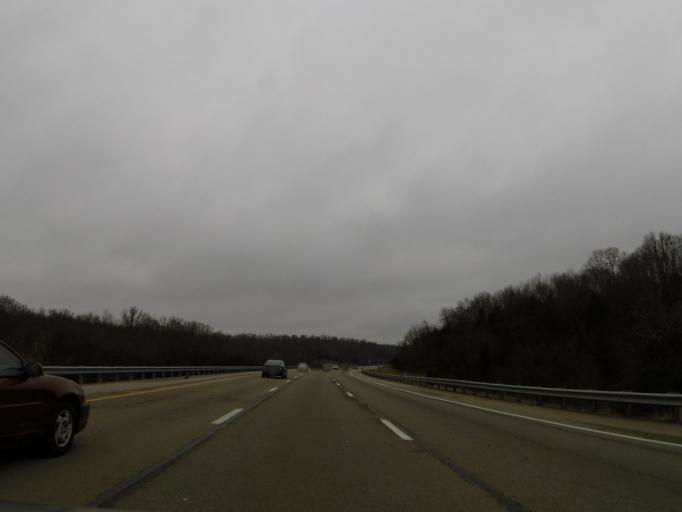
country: US
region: Kentucky
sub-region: Grant County
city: Williamstown
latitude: 38.4835
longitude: -84.5828
